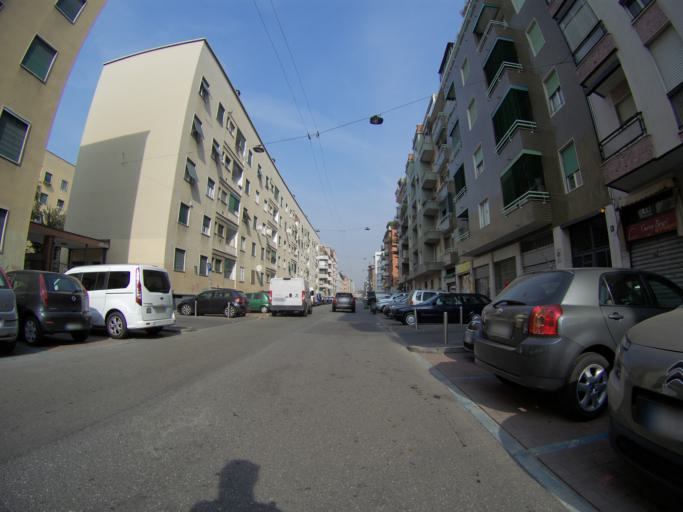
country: IT
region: Lombardy
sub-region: Citta metropolitana di Milano
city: Milano
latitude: 45.4692
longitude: 9.2325
